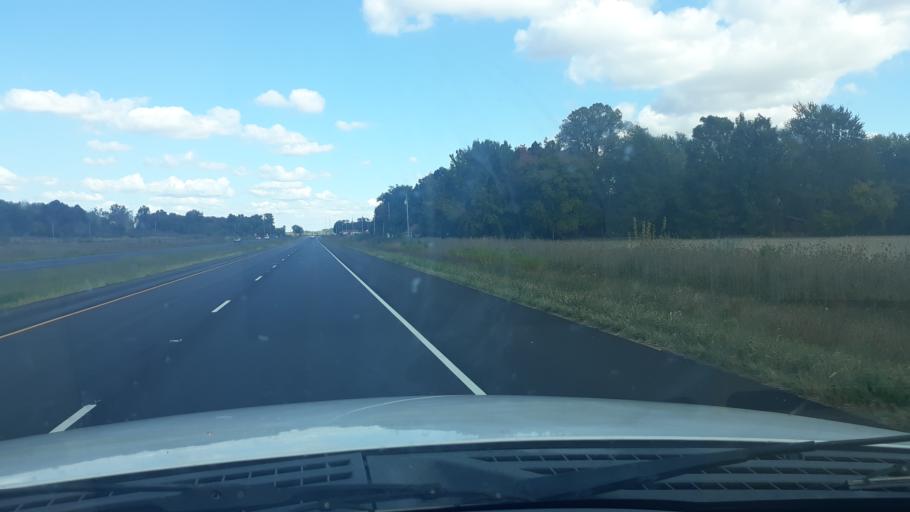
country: US
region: Illinois
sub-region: Saline County
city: Eldorado
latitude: 37.7833
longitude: -88.4909
